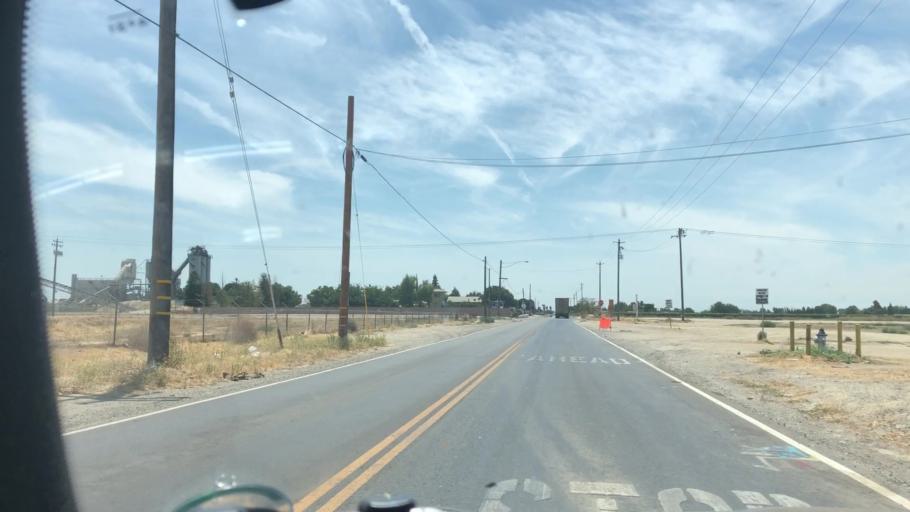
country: US
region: California
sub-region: Fresno County
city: Easton
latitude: 36.6793
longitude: -119.7547
